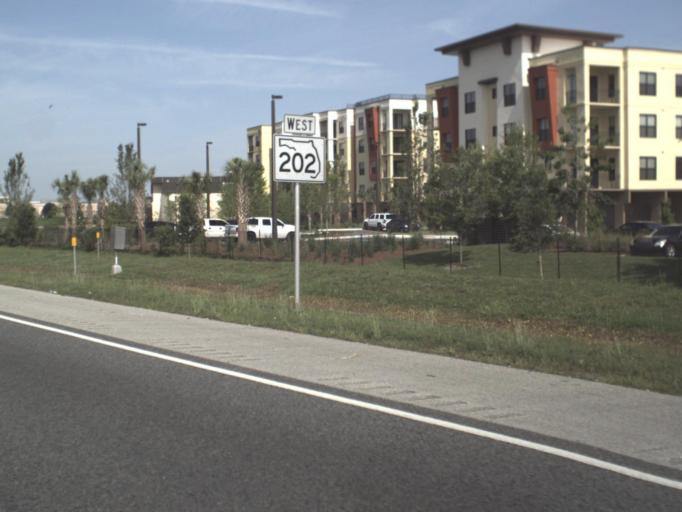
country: US
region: Florida
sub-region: Duval County
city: Jacksonville Beach
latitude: 30.2510
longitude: -81.5262
